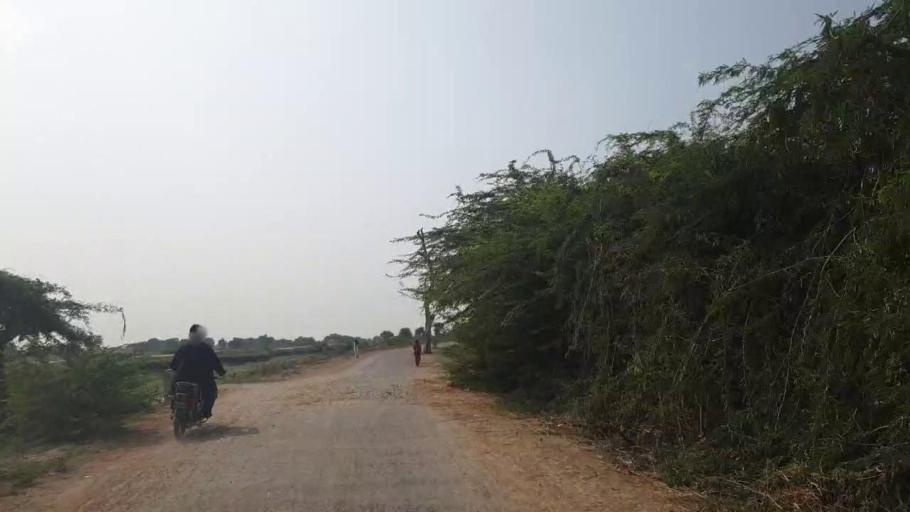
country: PK
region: Sindh
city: Talhar
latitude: 24.7754
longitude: 68.7744
